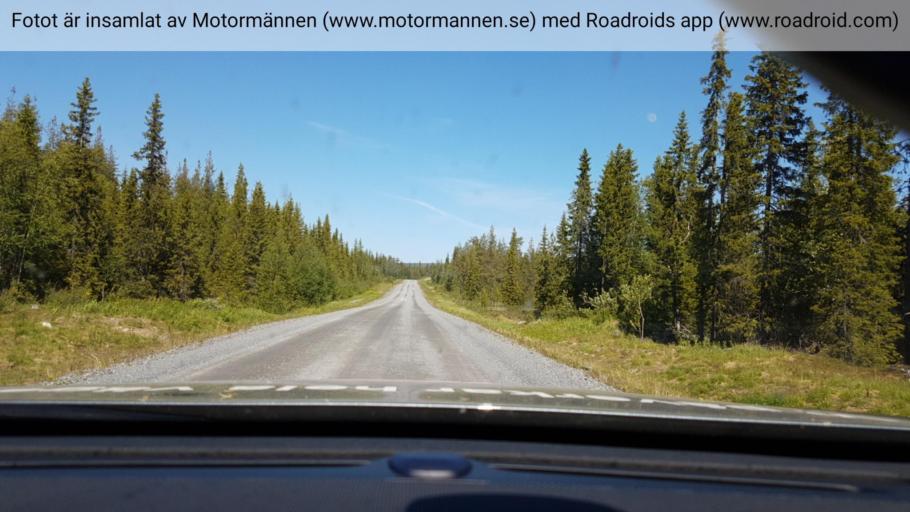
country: SE
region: Vaesterbotten
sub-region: Vilhelmina Kommun
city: Sjoberg
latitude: 64.6937
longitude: 15.7573
